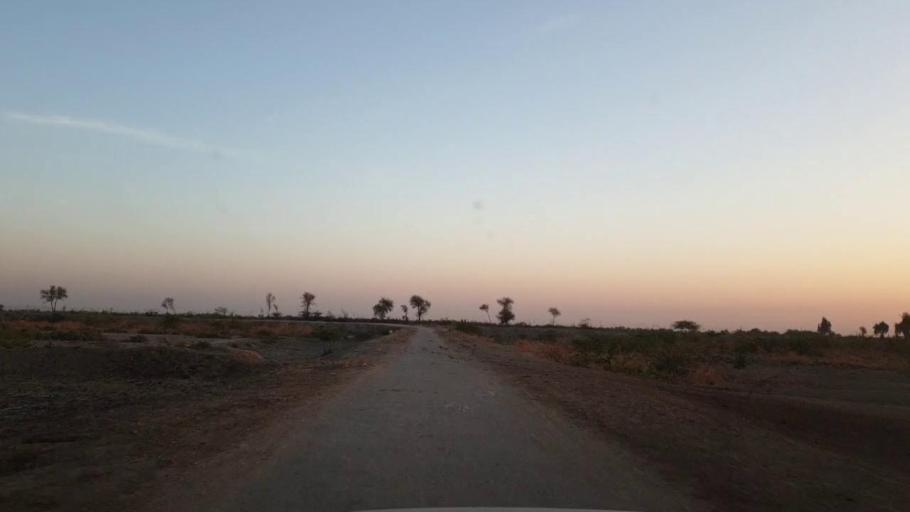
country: PK
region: Sindh
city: Samaro
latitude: 25.1496
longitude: 69.4257
